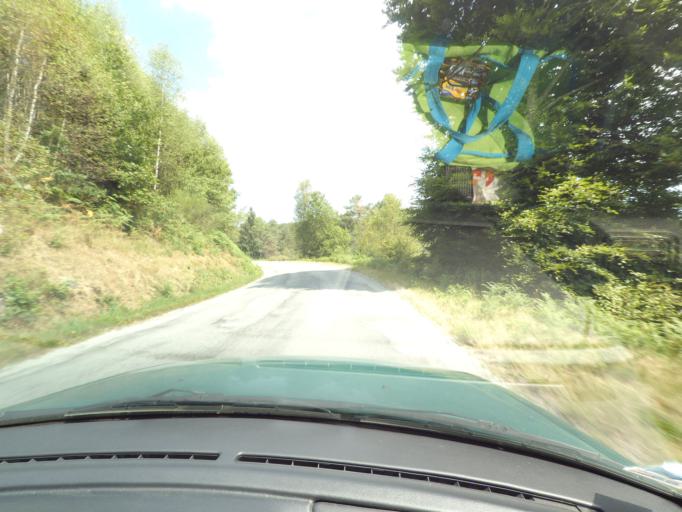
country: FR
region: Limousin
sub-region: Departement de la Correze
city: Bugeat
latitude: 45.7475
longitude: 1.9223
